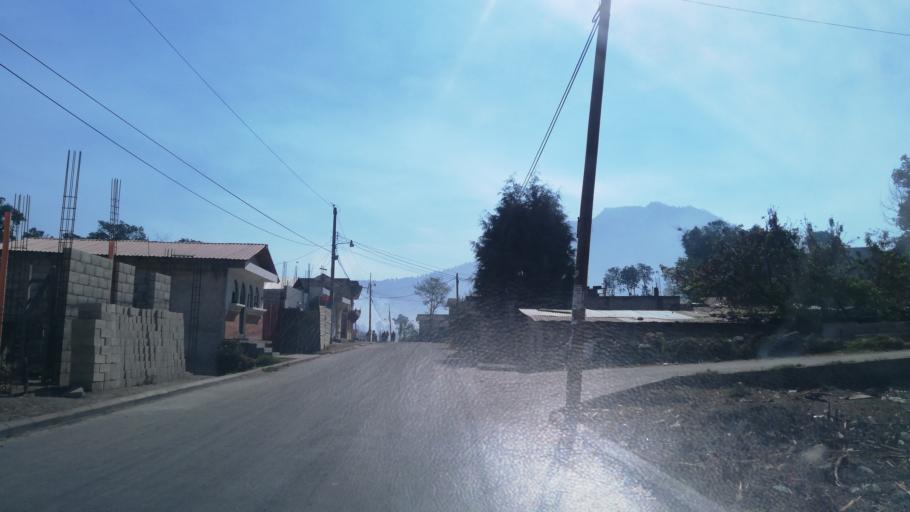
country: GT
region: Quetzaltenango
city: Quetzaltenango
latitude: 14.8053
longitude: -91.5528
